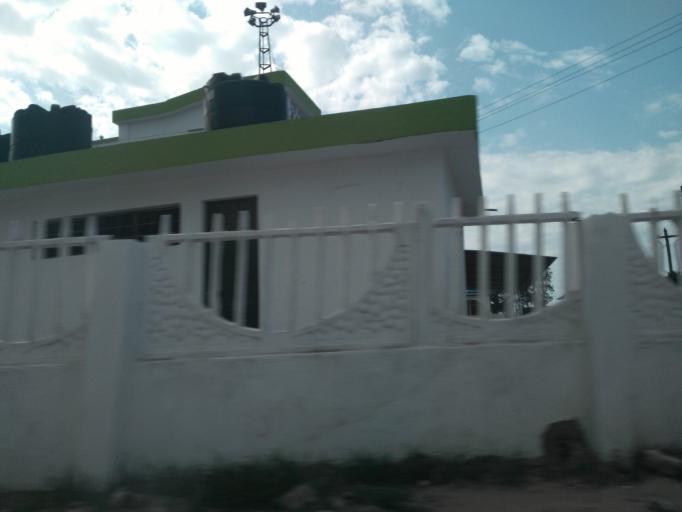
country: TZ
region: Dar es Salaam
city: Magomeni
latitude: -6.7603
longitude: 39.2694
